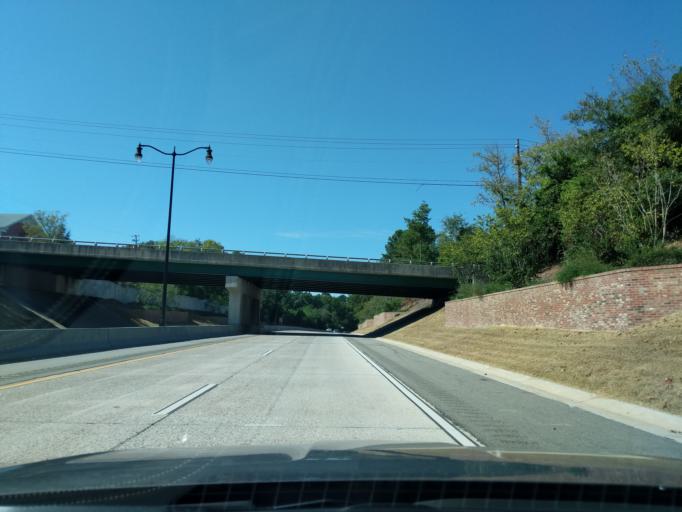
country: US
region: Georgia
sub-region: Richmond County
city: Augusta
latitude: 33.4869
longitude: -82.0062
